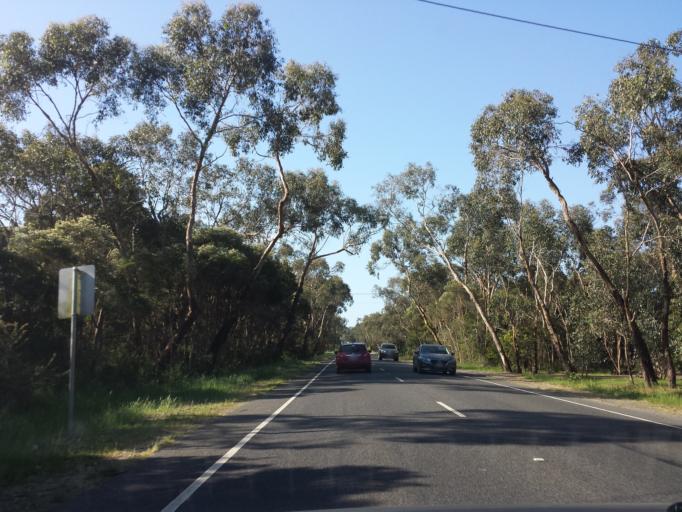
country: AU
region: Victoria
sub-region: Yarra Ranges
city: Belgrave South
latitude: -37.9589
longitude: 145.3454
